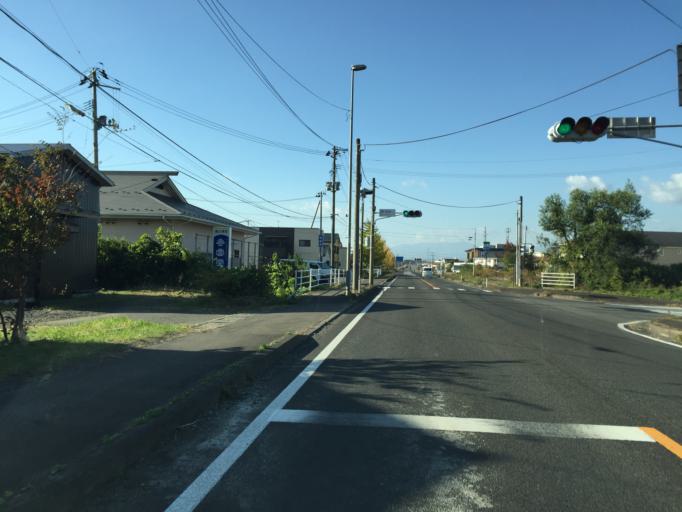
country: JP
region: Fukushima
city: Yanagawamachi-saiwaicho
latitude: 37.8791
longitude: 140.5522
